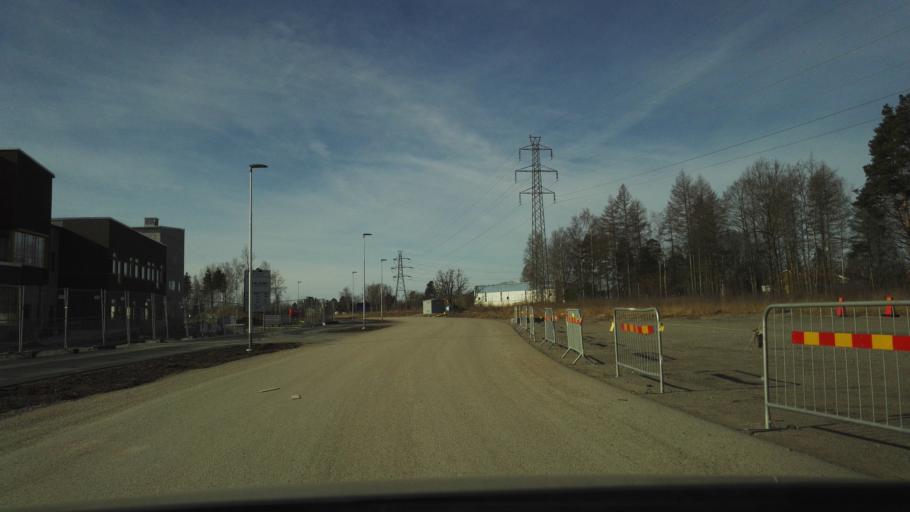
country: SE
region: Kronoberg
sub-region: Vaxjo Kommun
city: Vaexjoe
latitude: 56.8775
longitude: 14.7453
